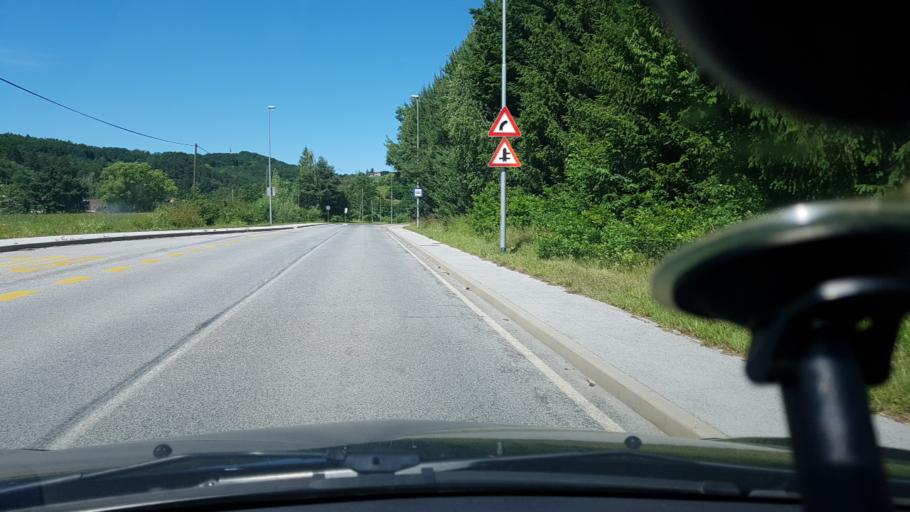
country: SI
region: Oplotnica
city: Oplotnica
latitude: 46.3817
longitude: 15.5102
